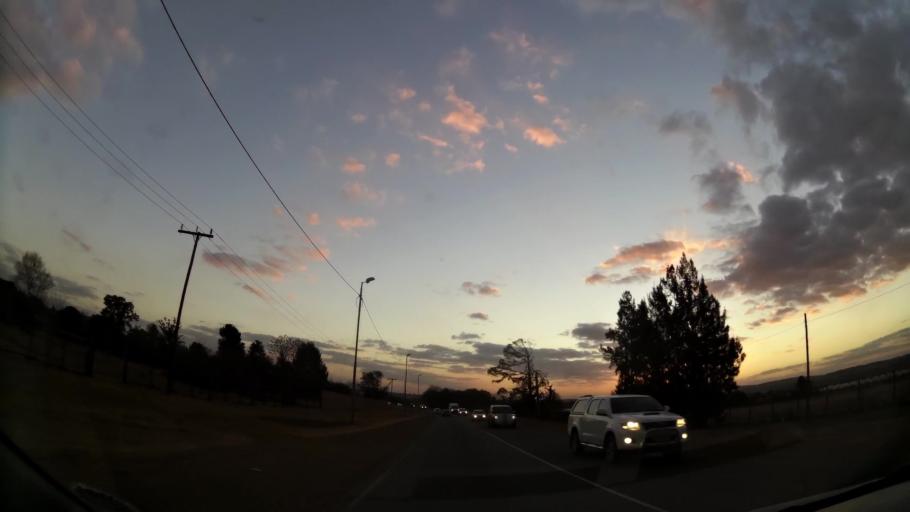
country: ZA
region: Gauteng
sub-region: West Rand District Municipality
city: Krugersdorp
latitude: -26.0341
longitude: 27.7286
